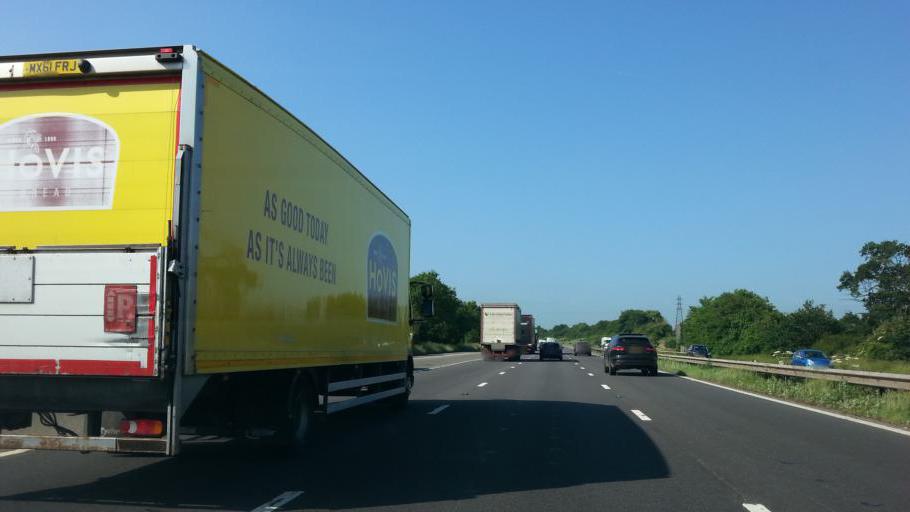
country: GB
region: England
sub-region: Gloucestershire
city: Stonehouse
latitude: 51.7563
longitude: -2.3269
